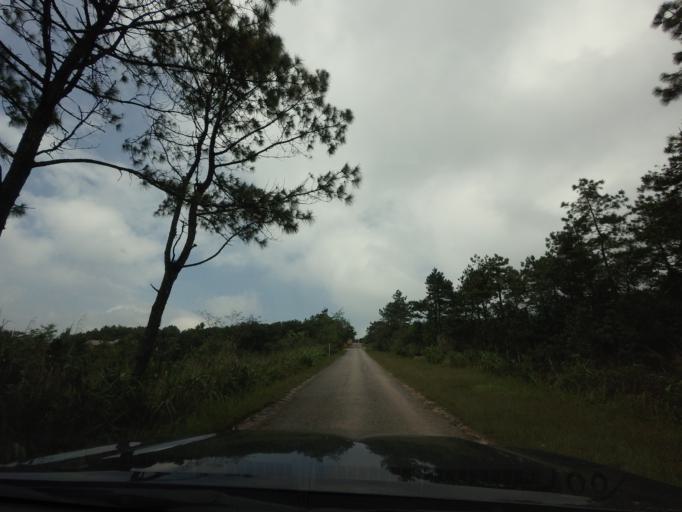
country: TH
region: Loei
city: Phu Ruea
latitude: 17.5071
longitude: 101.3475
